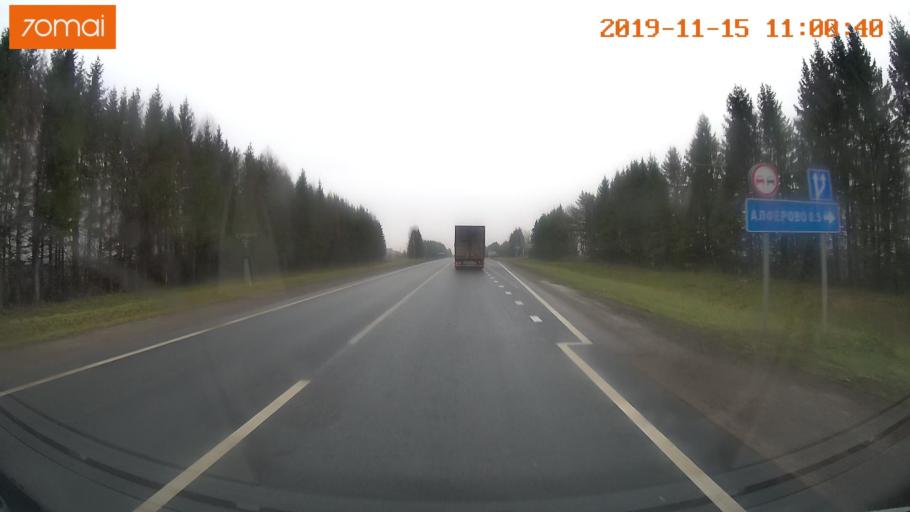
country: RU
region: Vologda
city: Chebsara
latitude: 59.1362
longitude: 38.9040
